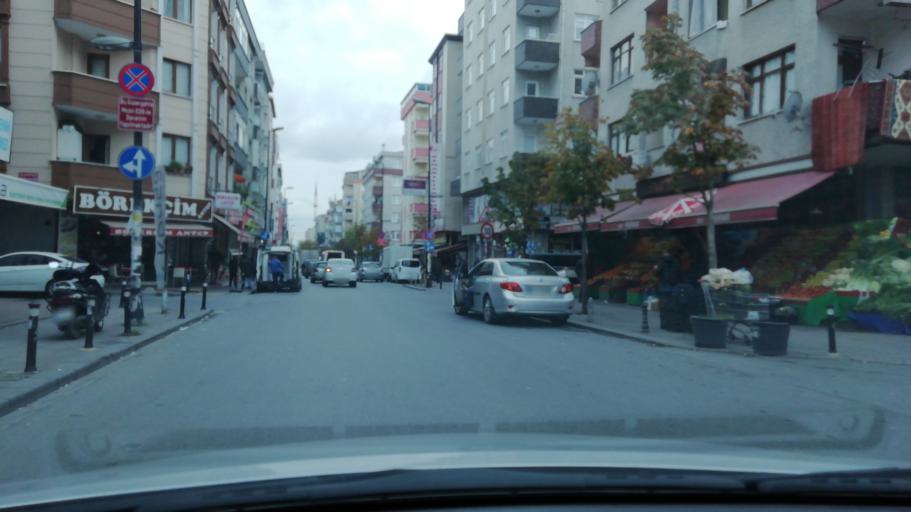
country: TR
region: Istanbul
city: Bahcelievler
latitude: 41.0081
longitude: 28.8387
